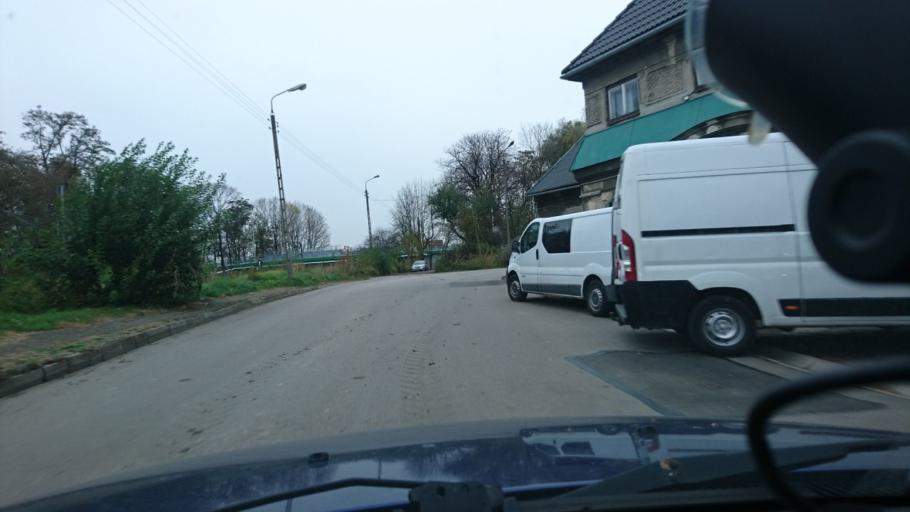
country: PL
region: Silesian Voivodeship
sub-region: Bielsko-Biala
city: Bielsko-Biala
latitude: 49.8338
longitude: 19.0384
